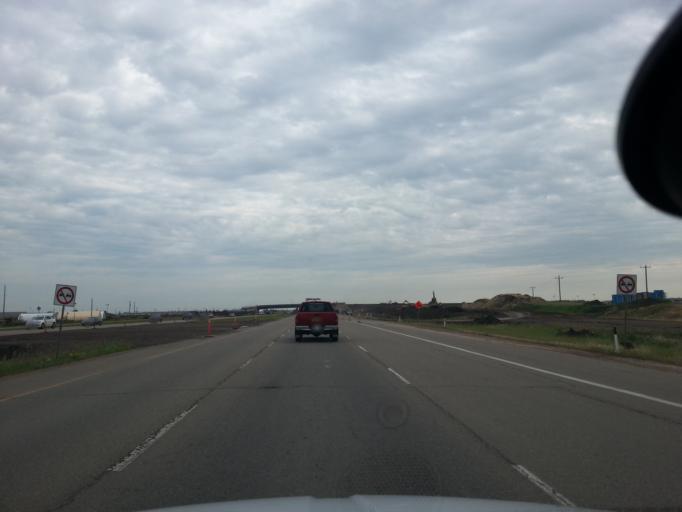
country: CA
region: Alberta
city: Sherwood Park
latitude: 53.5700
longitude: -113.3044
